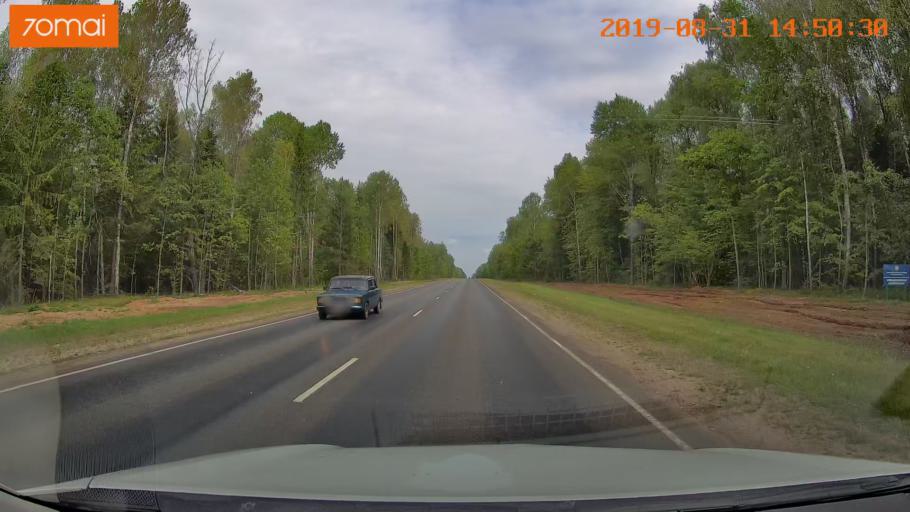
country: RU
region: Kaluga
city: Spas-Demensk
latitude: 54.2618
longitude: 33.7912
